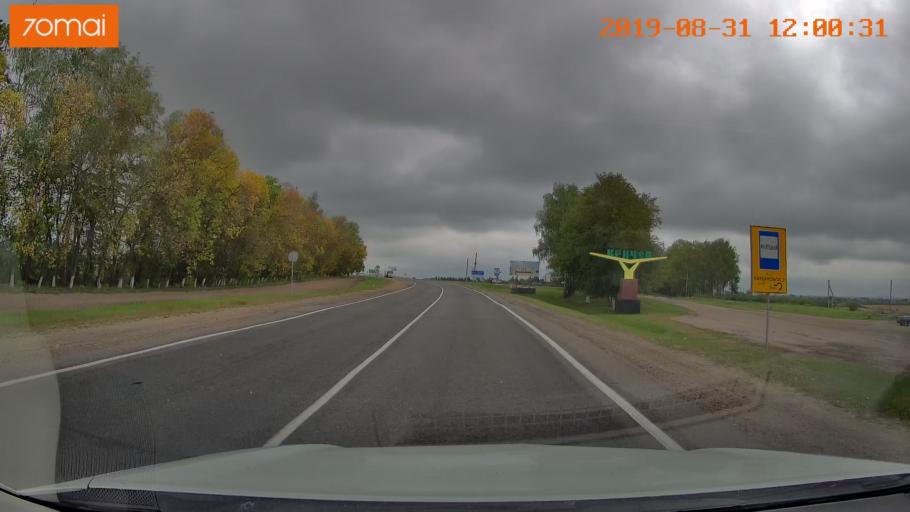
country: BY
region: Mogilev
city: Horad Krychaw
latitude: 53.6795
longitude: 31.6824
